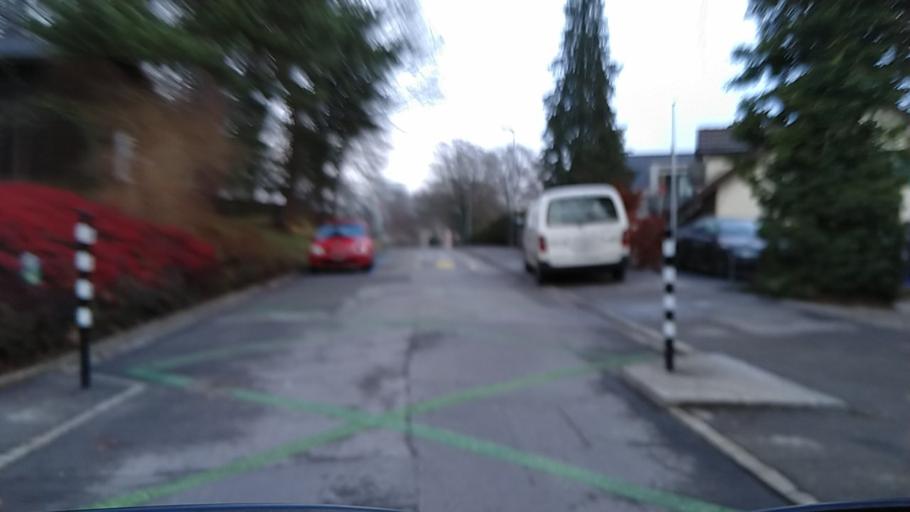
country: CH
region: Bern
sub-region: Bern-Mittelland District
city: Koniz
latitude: 46.9418
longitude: 7.3814
